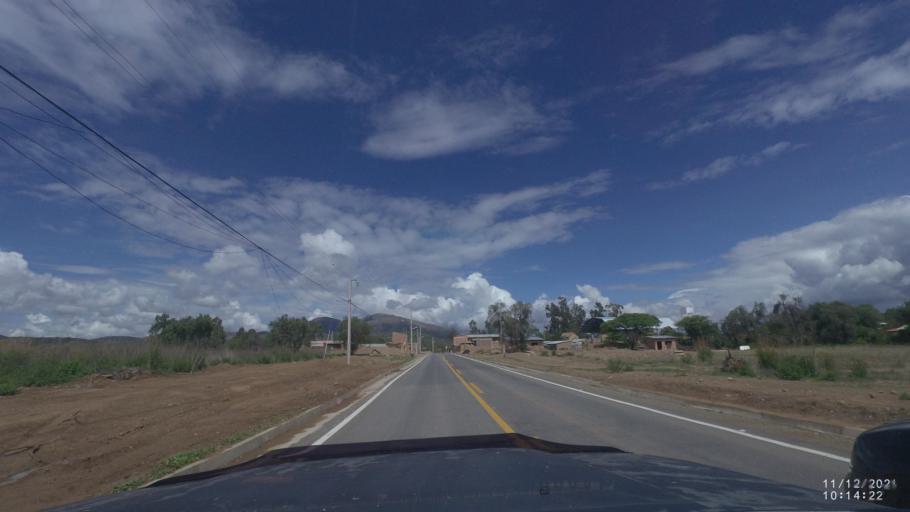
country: BO
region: Cochabamba
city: Tarata
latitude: -17.6156
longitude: -66.0181
